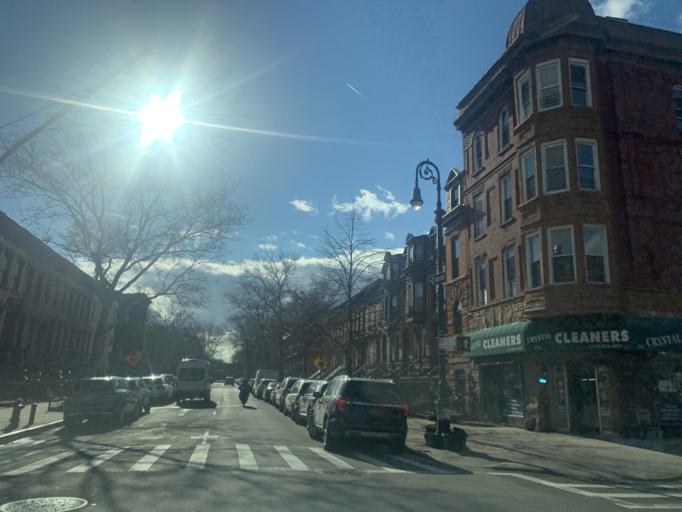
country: US
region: New York
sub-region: Kings County
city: Brooklyn
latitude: 40.6840
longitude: -73.9323
